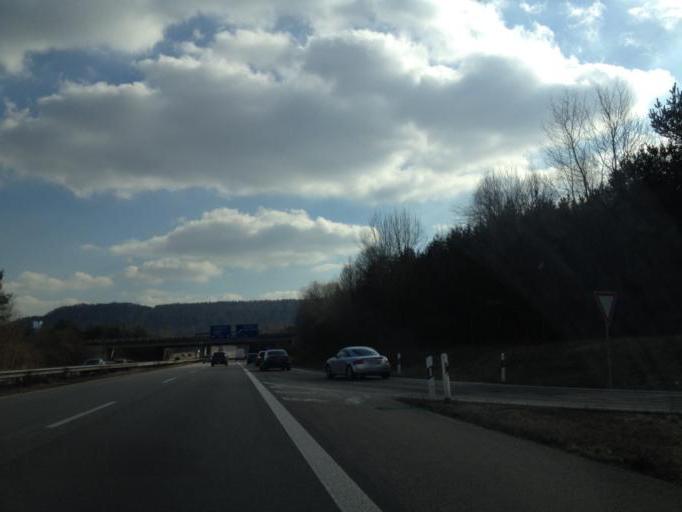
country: DE
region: Rheinland-Pfalz
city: Steinwenden
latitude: 49.4188
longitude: 7.5267
